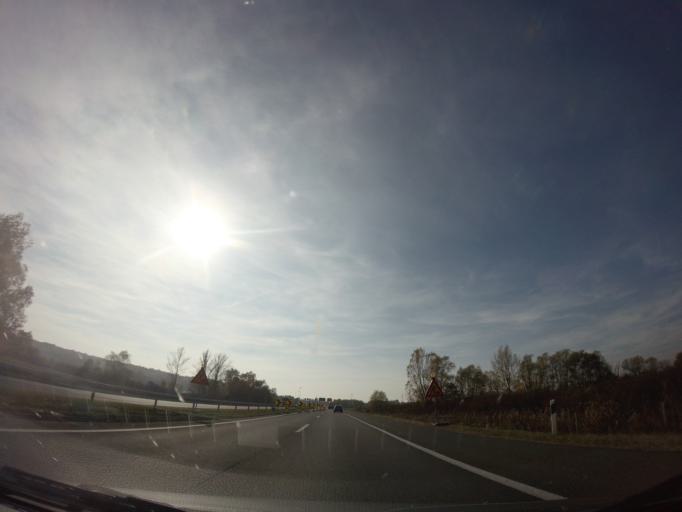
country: HR
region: Grad Zagreb
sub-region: Sesvete
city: Sesvete
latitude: 45.8530
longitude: 16.1526
